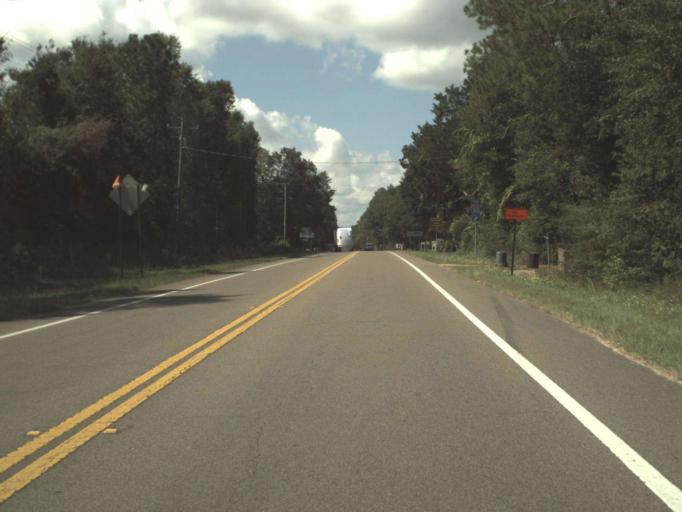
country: US
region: Florida
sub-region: Walton County
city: Freeport
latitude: 30.4712
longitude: -85.9601
